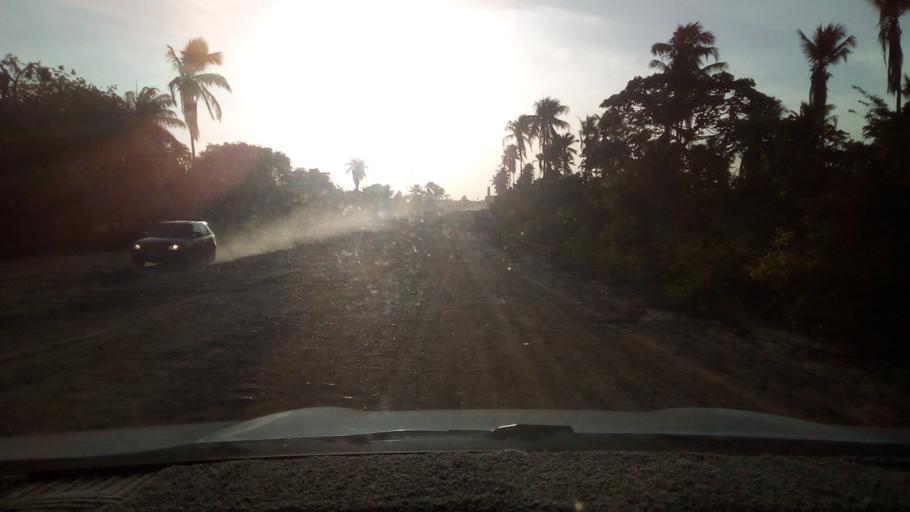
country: BR
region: Paraiba
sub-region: Conde
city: Conde
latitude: -7.1948
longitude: -34.8906
